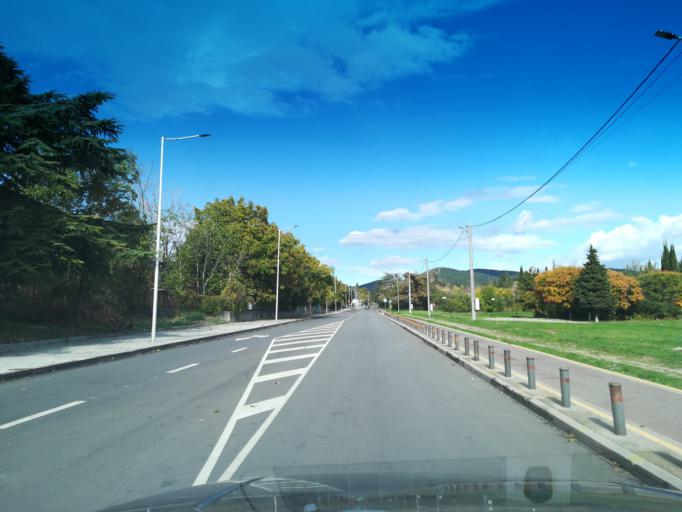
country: BG
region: Stara Zagora
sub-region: Obshtina Stara Zagora
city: Stara Zagora
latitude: 42.4392
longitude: 25.6356
